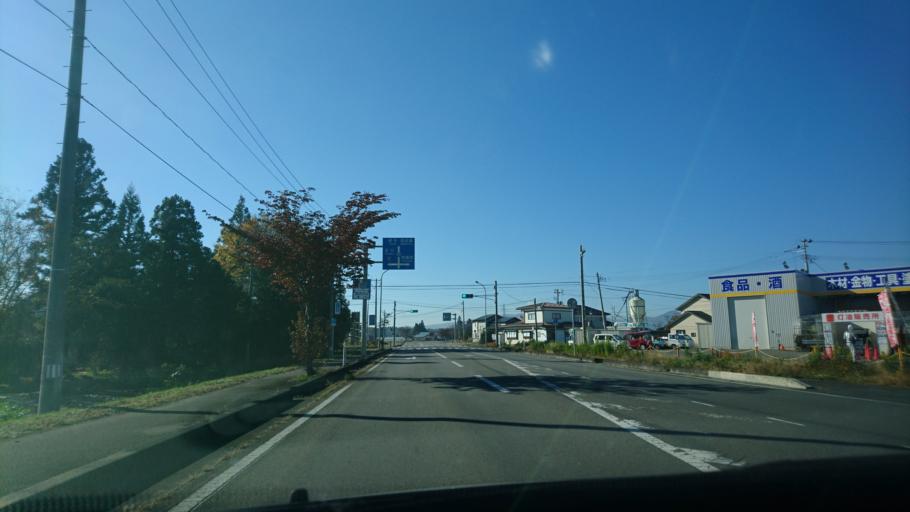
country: JP
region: Iwate
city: Mizusawa
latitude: 39.1317
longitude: 141.0655
